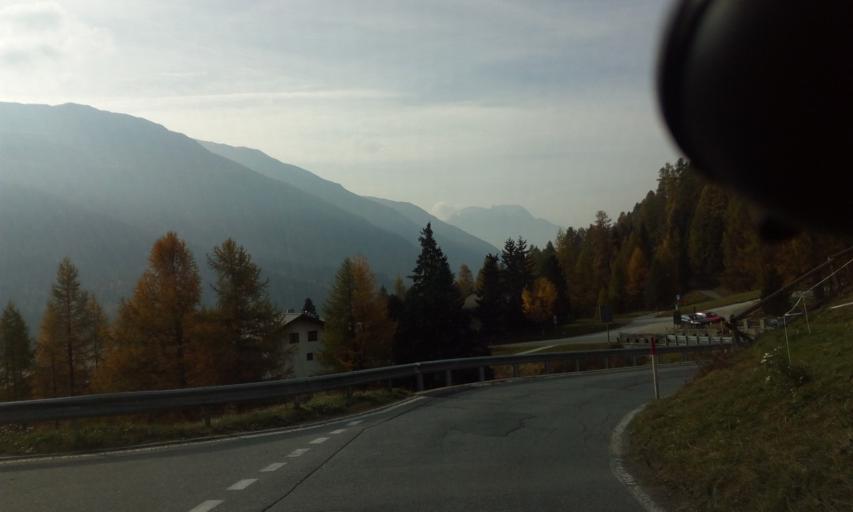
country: CH
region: Grisons
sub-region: Maloja District
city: Ponte
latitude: 46.5805
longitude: 9.9200
